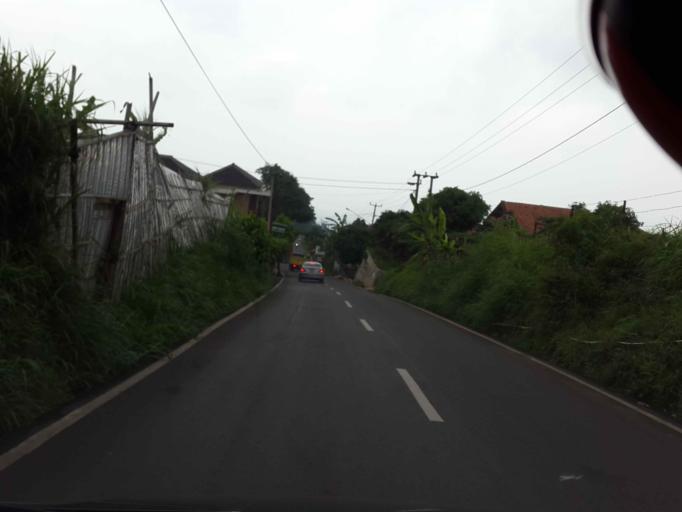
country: ID
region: West Java
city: Cimahi
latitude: -6.8276
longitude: 107.5239
